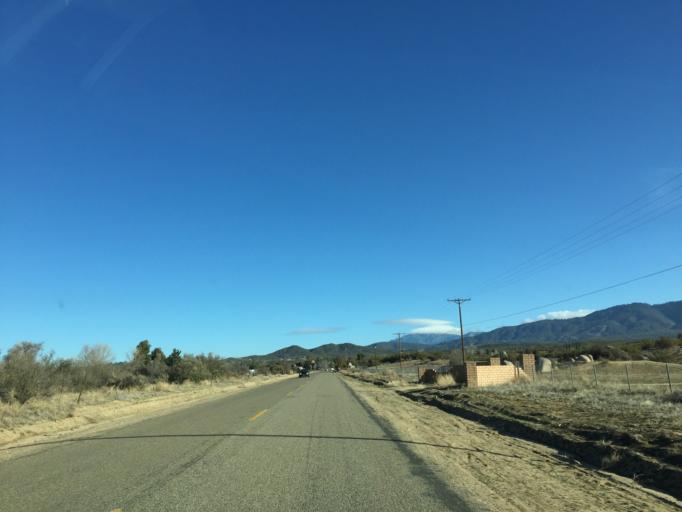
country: US
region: California
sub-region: Riverside County
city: Anza
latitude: 33.5556
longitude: -116.7359
